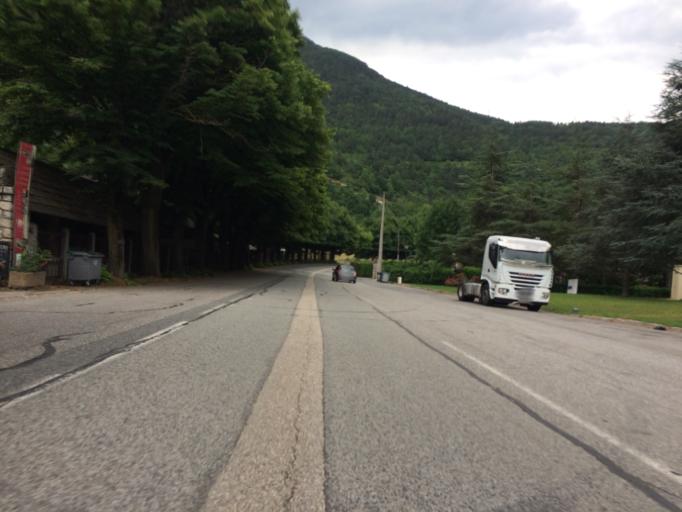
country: FR
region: Provence-Alpes-Cote d'Azur
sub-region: Departement des Alpes-Maritimes
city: Tende
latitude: 44.0773
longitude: 7.5988
